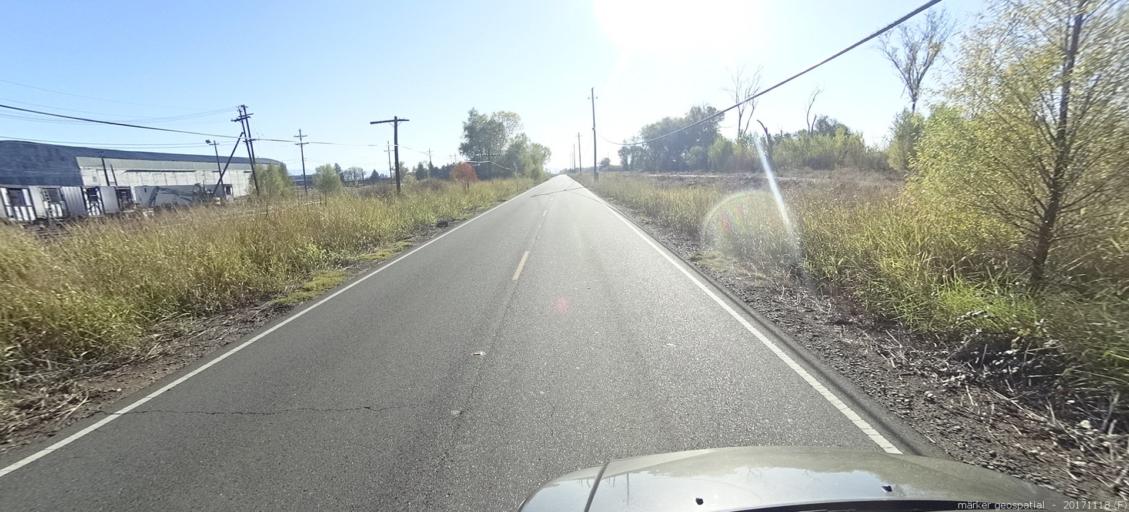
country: US
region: California
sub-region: Shasta County
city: Anderson
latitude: 40.4354
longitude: -122.2793
